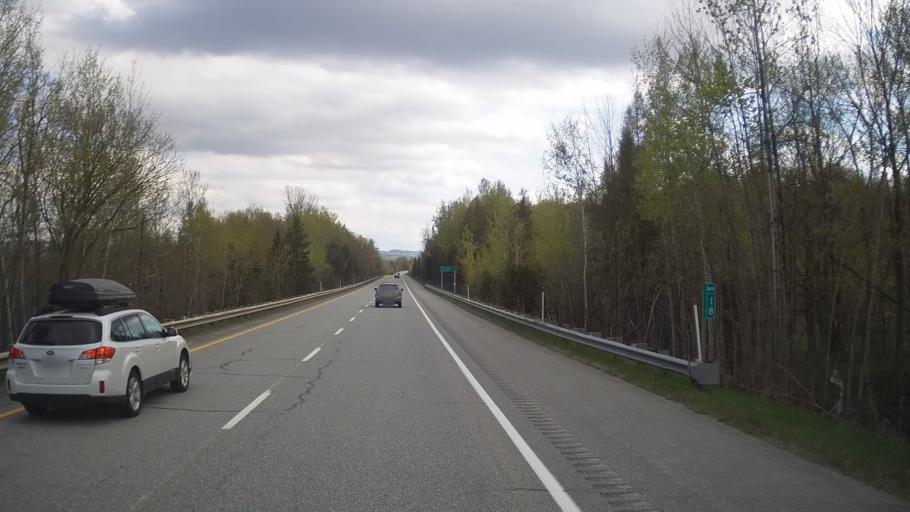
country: CA
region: Quebec
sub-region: Estrie
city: Magog
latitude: 45.1635
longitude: -72.0652
